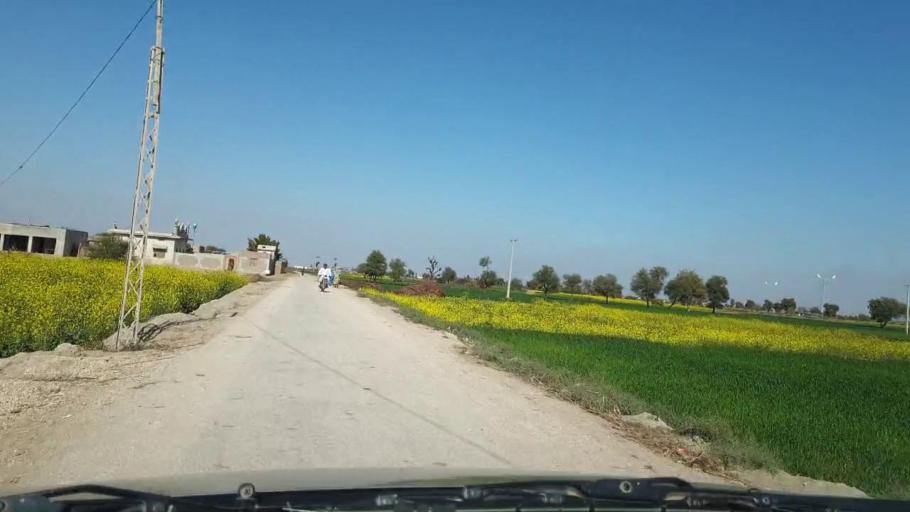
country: PK
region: Sindh
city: Khadro
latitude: 26.1437
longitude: 68.7952
